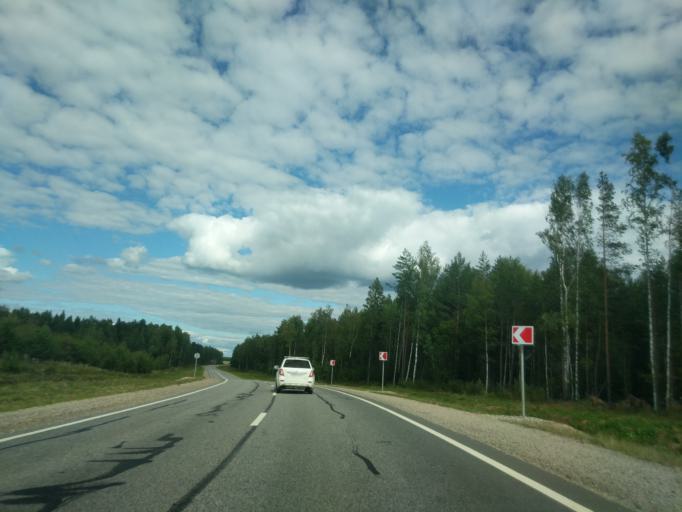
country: RU
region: Kostroma
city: Ostrovskoye
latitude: 57.8088
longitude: 42.4156
